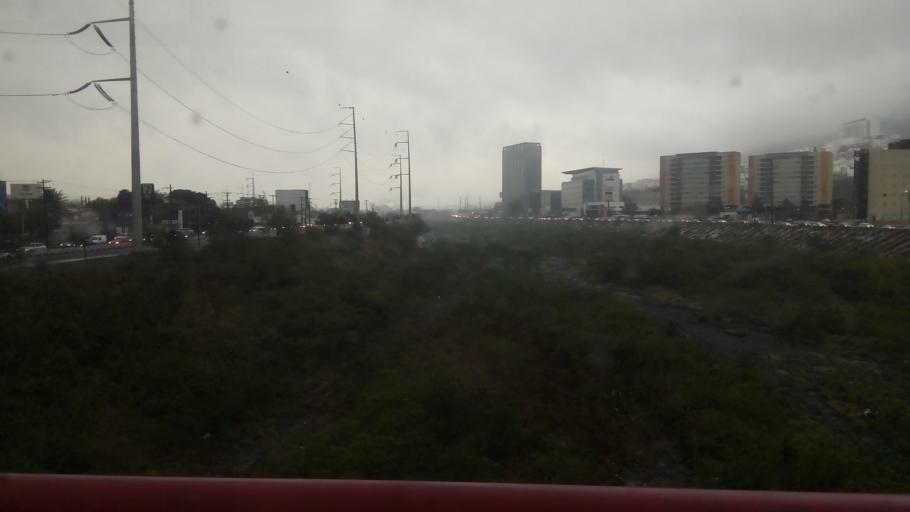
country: MX
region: Nuevo Leon
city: Garza Garcia
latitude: 25.6700
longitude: -100.3862
